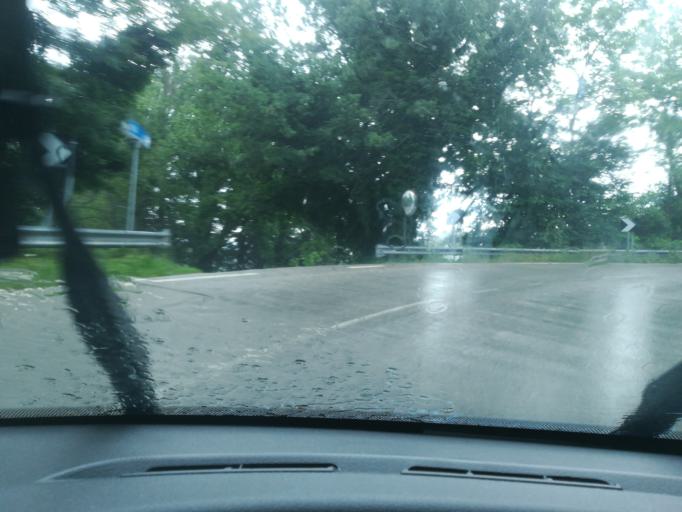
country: IT
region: The Marches
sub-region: Province of Fermo
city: Amandola
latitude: 43.0001
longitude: 13.3352
